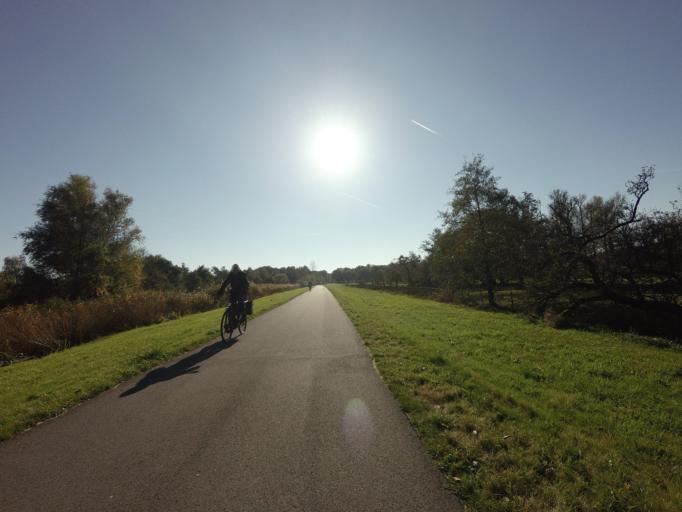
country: NL
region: North Holland
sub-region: Gemeente Naarden
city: Naarden
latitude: 52.2886
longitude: 5.1432
